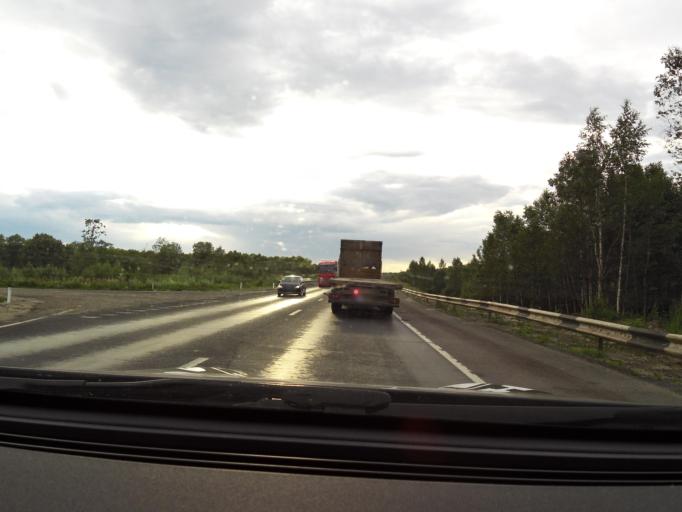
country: RU
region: Vladimir
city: Raduzhnyy
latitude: 56.0600
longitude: 40.3788
